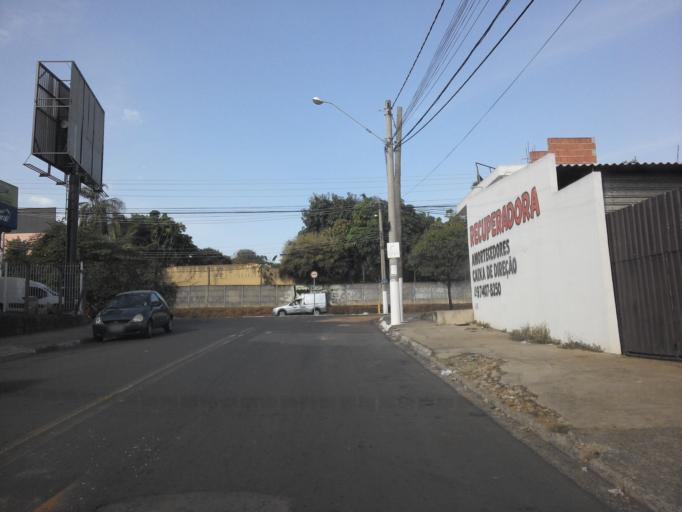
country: BR
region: Sao Paulo
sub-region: Hortolandia
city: Hortolandia
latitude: -22.9022
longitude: -47.2301
